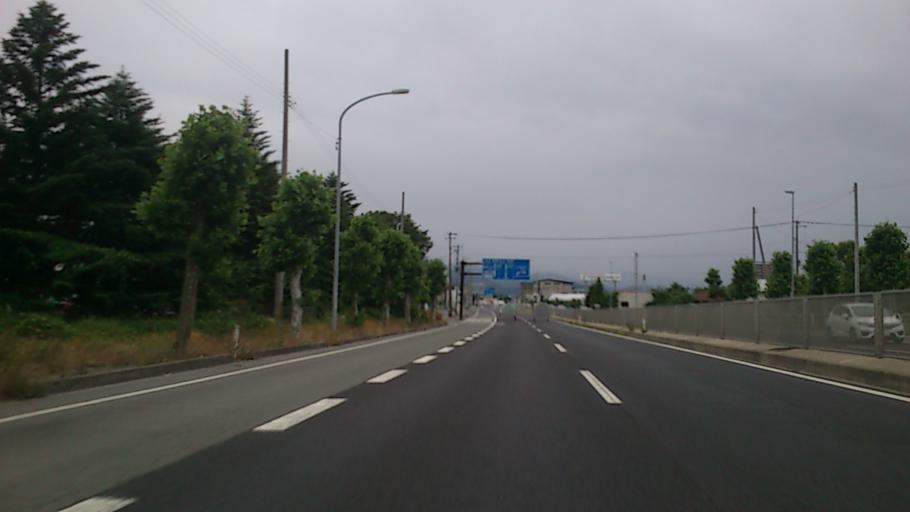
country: JP
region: Yamagata
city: Tendo
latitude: 38.3163
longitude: 140.3625
